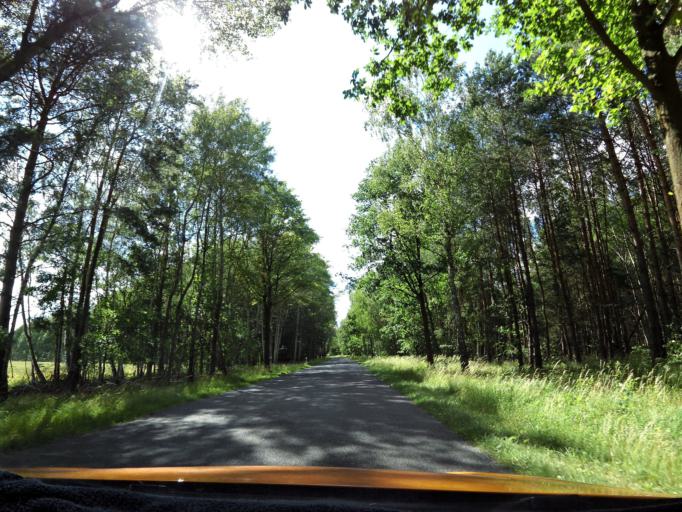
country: DE
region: Brandenburg
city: Erkner
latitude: 52.3193
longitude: 13.7606
